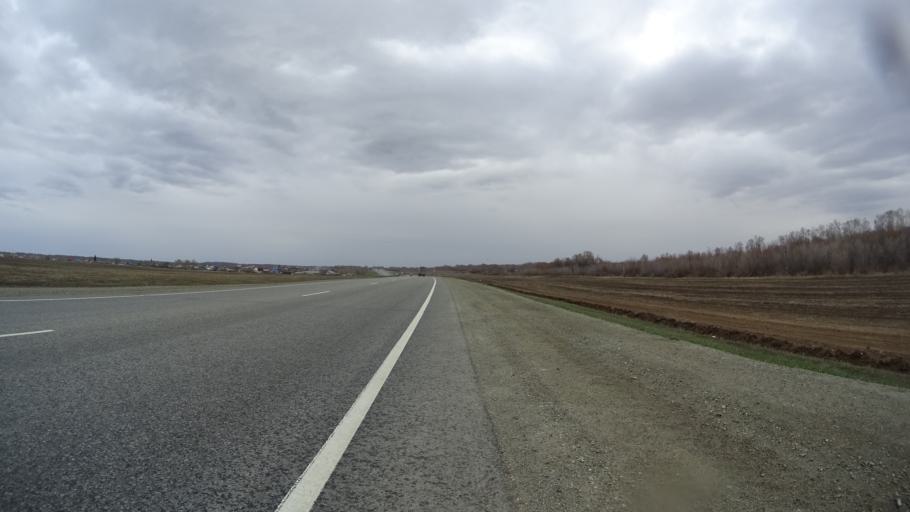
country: RU
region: Chelyabinsk
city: Krasnogorskiy
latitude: 54.6803
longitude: 61.2470
